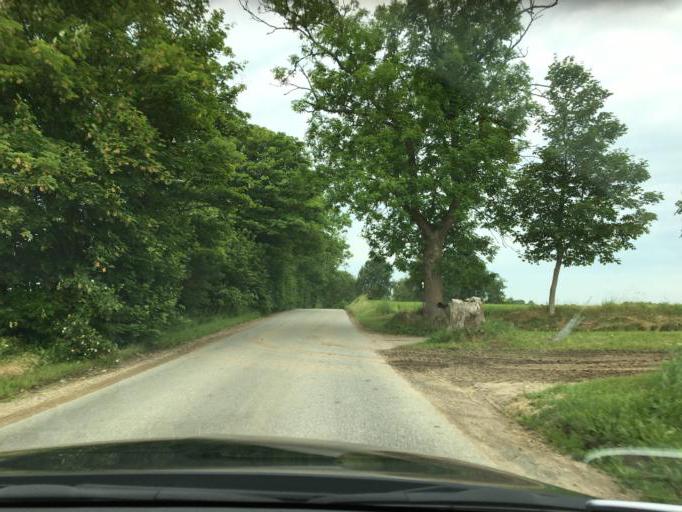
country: DK
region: South Denmark
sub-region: Vejle Kommune
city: Vejle
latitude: 55.6163
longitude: 9.5468
